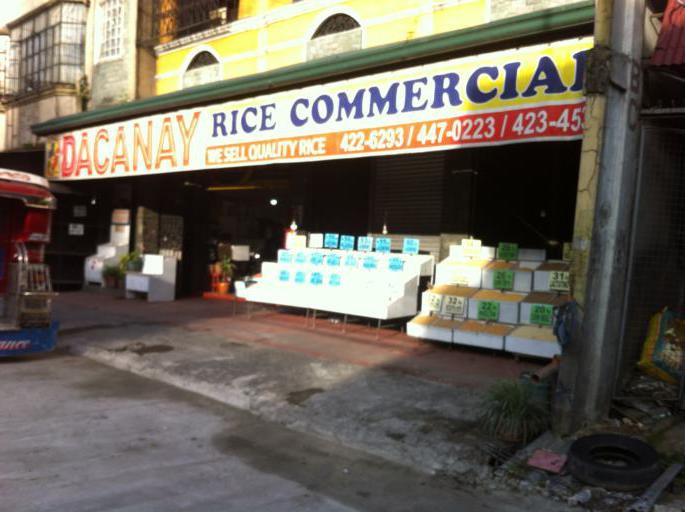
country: PH
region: Cordillera
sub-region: Baguio City
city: Baguio
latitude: 16.4326
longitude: 120.5976
